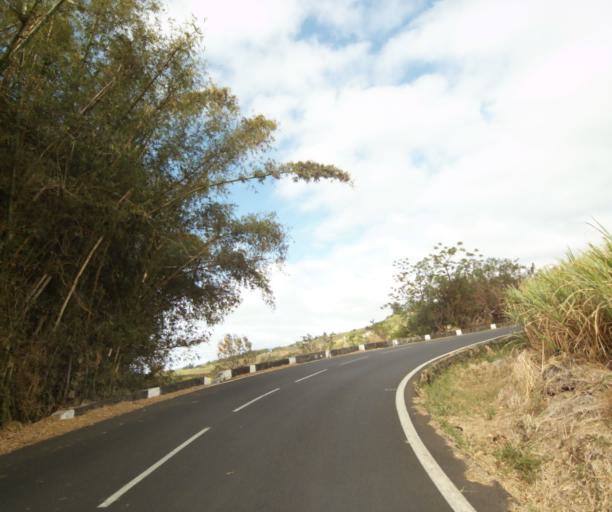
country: RE
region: Reunion
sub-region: Reunion
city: Saint-Paul
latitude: -21.0239
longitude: 55.3141
